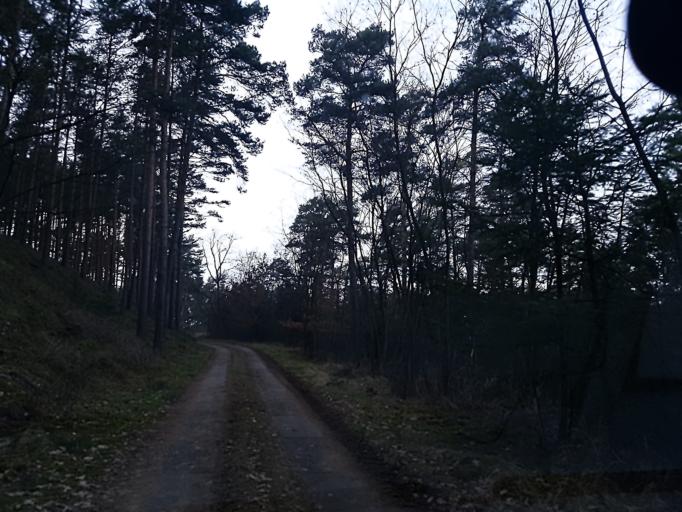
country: DE
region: Brandenburg
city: Wollin
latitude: 52.2565
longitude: 12.5180
